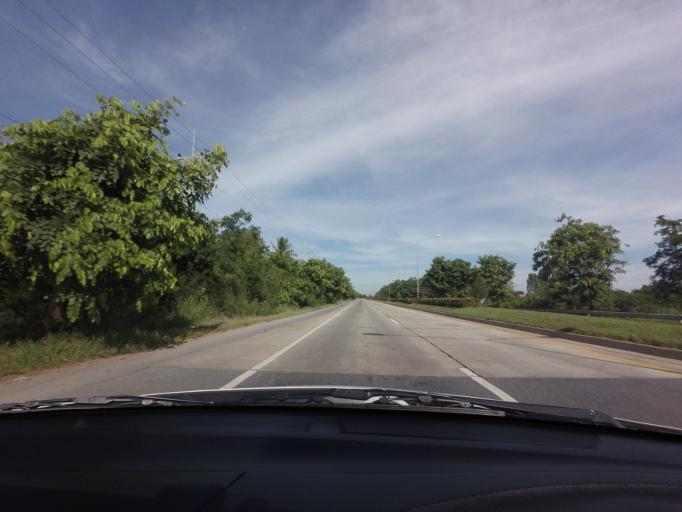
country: TH
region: Suphan Buri
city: Suphan Buri
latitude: 14.4558
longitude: 100.0634
